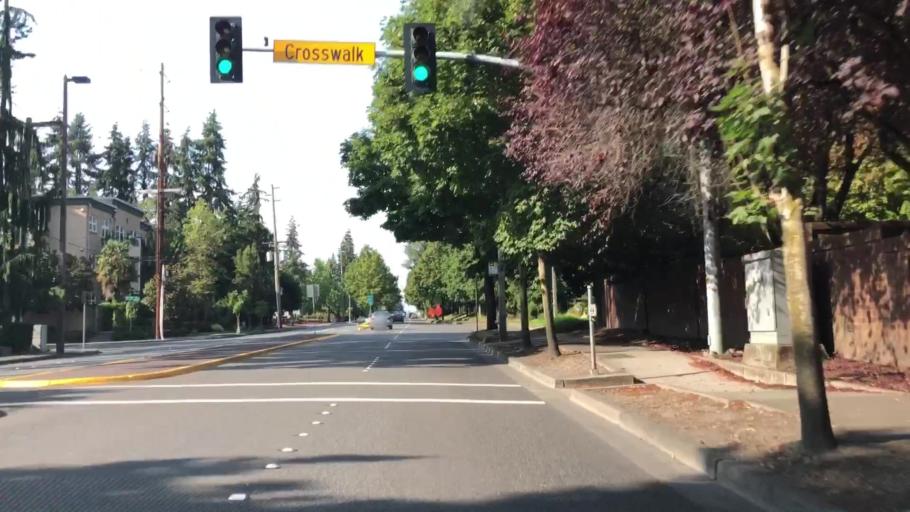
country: US
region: Washington
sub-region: King County
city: Bellevue
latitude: 47.6254
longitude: -122.2016
